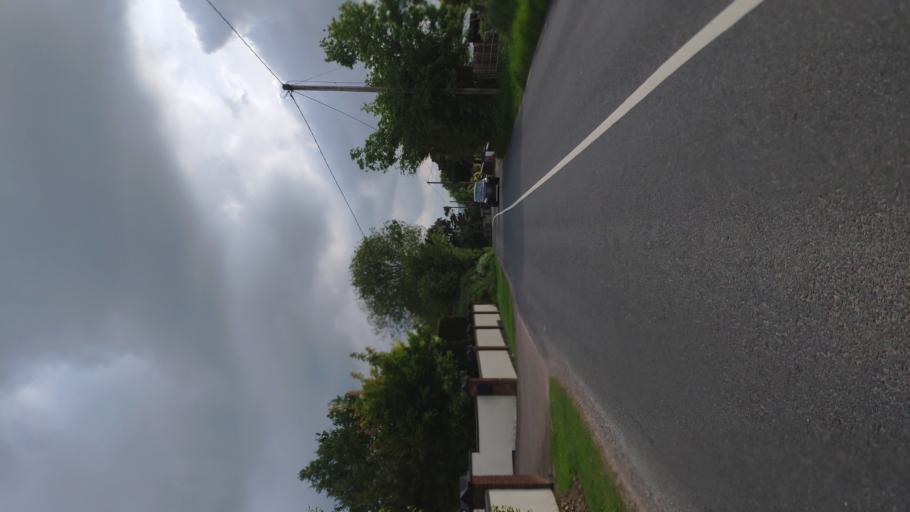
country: IE
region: Munster
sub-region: County Cork
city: Cork
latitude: 51.9417
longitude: -8.4462
